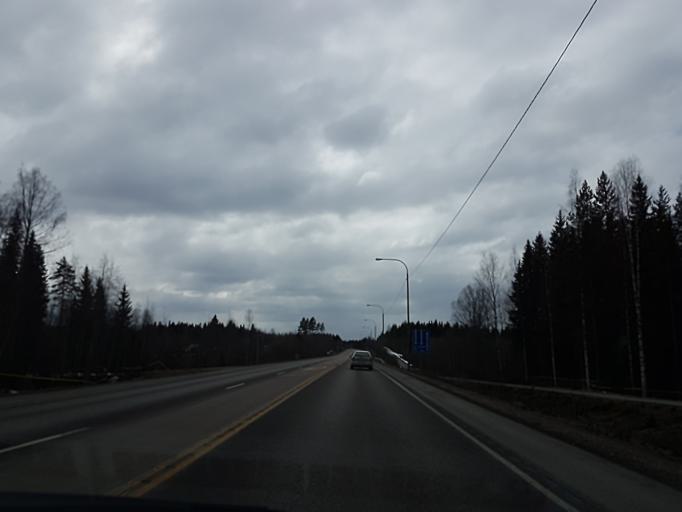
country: FI
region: Northern Savo
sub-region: Varkaus
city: Varkaus
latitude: 62.3960
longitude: 27.8192
